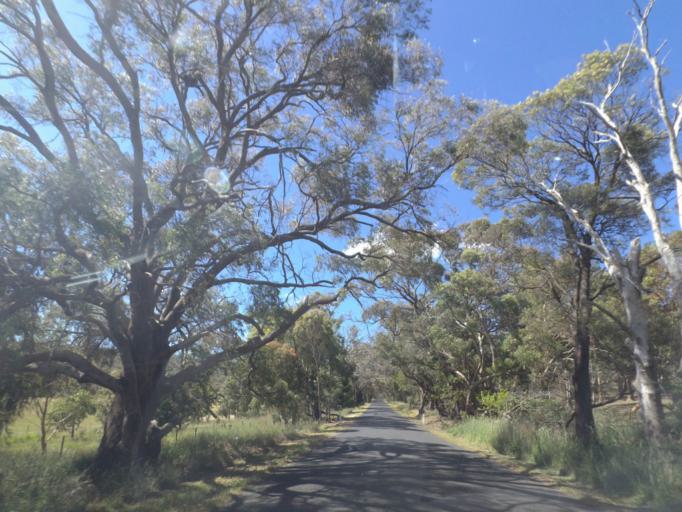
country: AU
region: Victoria
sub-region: Hume
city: Sunbury
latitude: -37.4267
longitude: 144.6166
